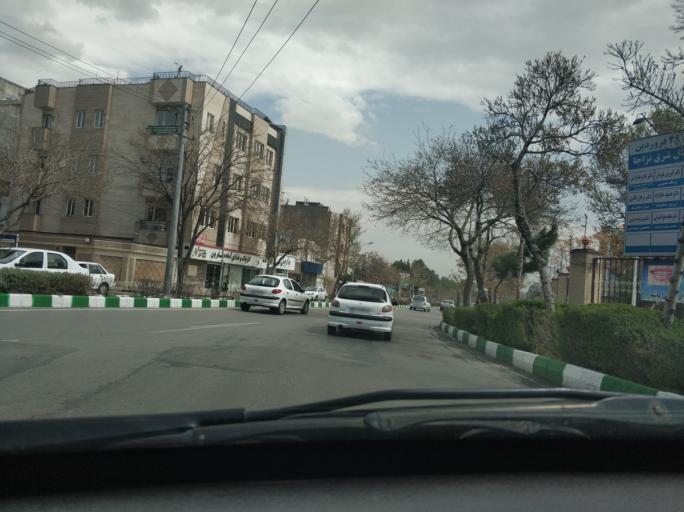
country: IR
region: Razavi Khorasan
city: Mashhad
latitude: 36.2845
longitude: 59.5782
